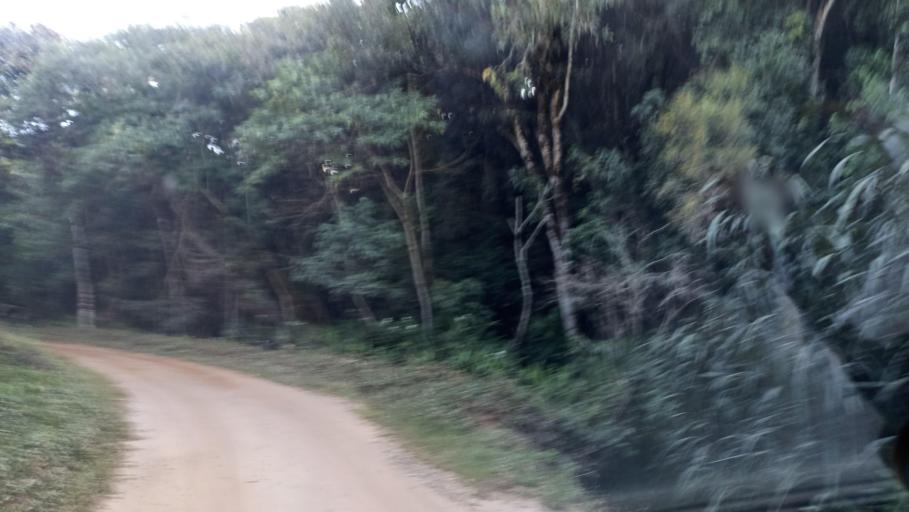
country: BR
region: Minas Gerais
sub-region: Ouro Preto
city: Ouro Preto
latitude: -20.2989
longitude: -43.5745
